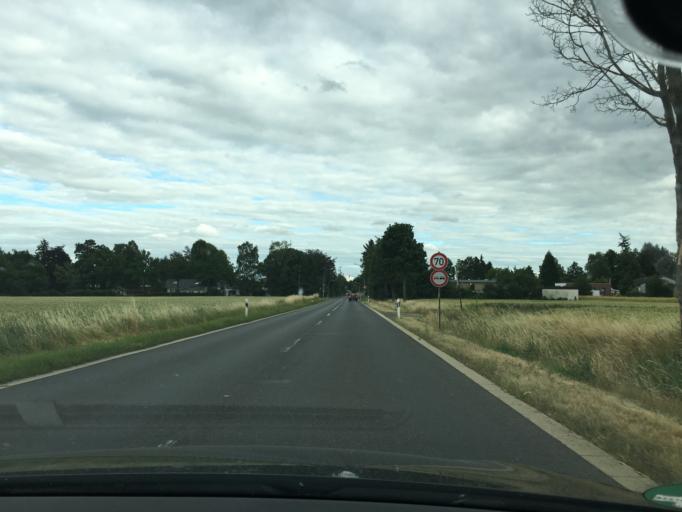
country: DE
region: North Rhine-Westphalia
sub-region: Regierungsbezirk Koln
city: Dueren
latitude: 50.7784
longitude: 6.4517
